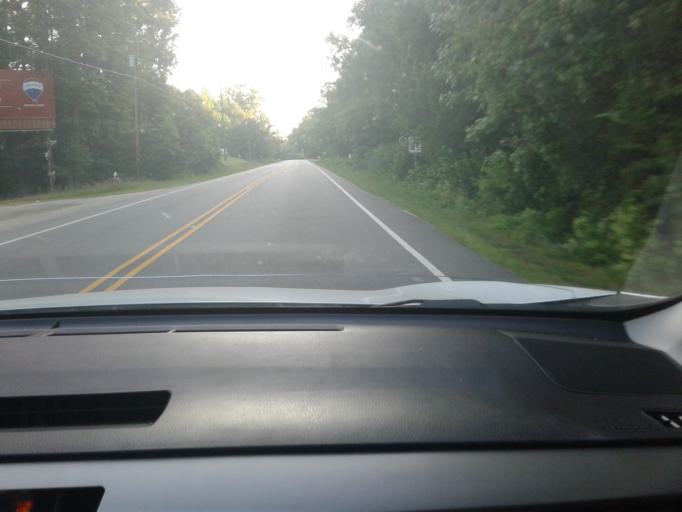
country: US
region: North Carolina
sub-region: Wake County
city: Fuquay-Varina
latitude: 35.5653
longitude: -78.8036
